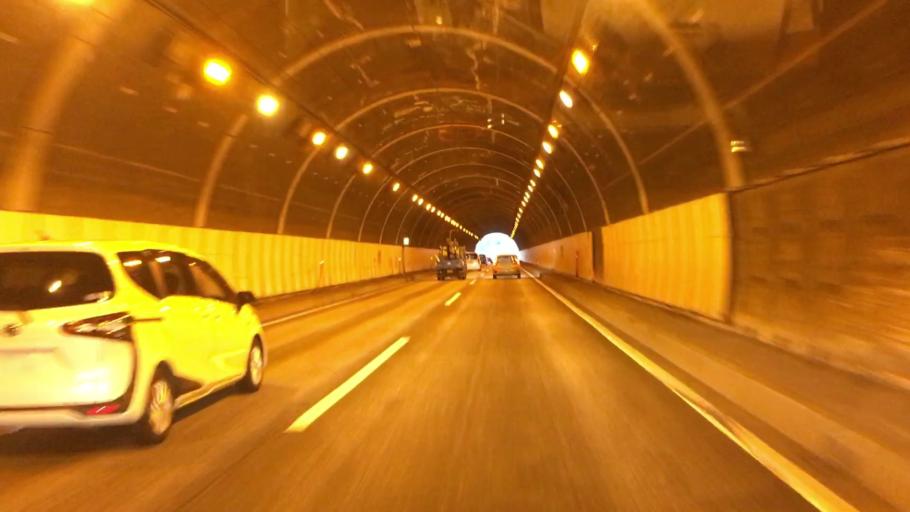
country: JP
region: Kanagawa
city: Kamakura
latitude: 35.3602
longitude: 139.5984
